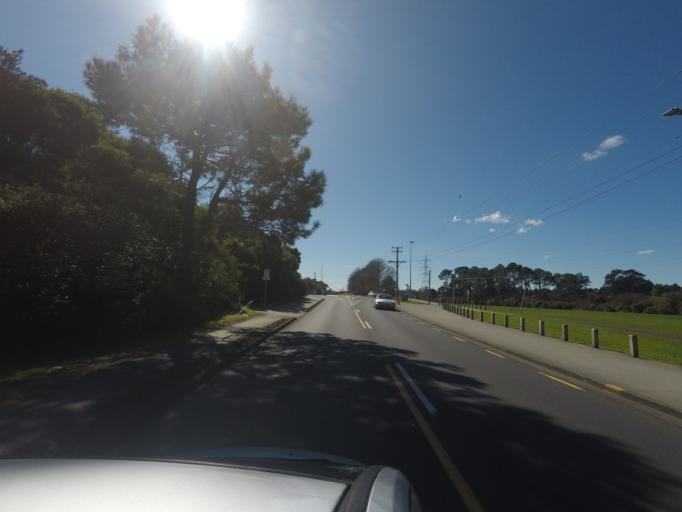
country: NZ
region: Auckland
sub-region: Auckland
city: Waitakere
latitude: -36.9236
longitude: 174.6906
